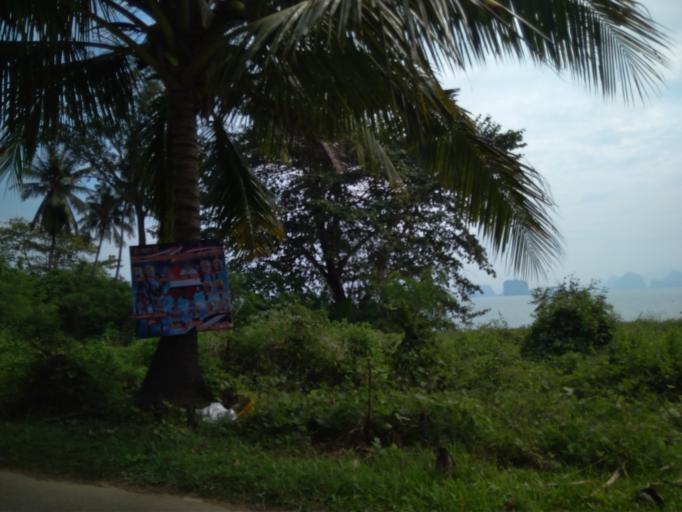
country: TH
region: Phangnga
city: Ko Yao
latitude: 8.1135
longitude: 98.6234
